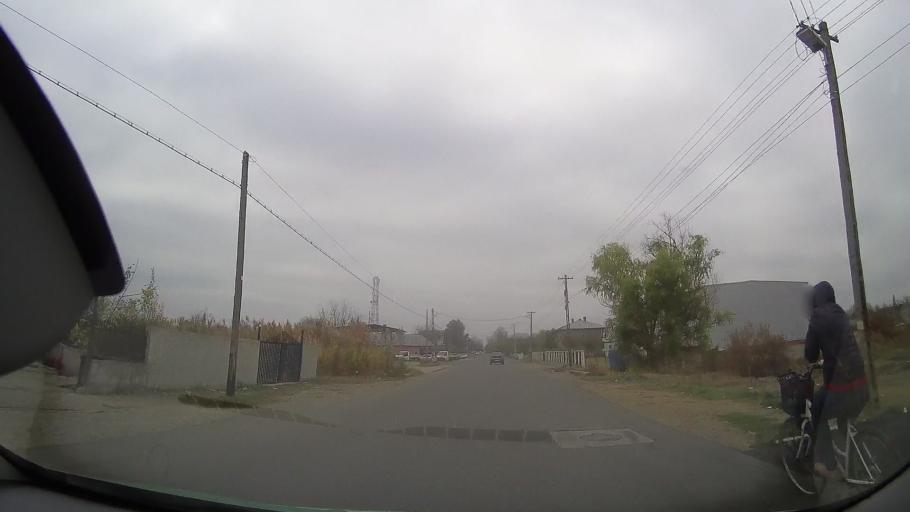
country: RO
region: Buzau
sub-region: Comuna Pogoanele
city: Pogoanele
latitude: 44.9195
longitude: 26.9922
